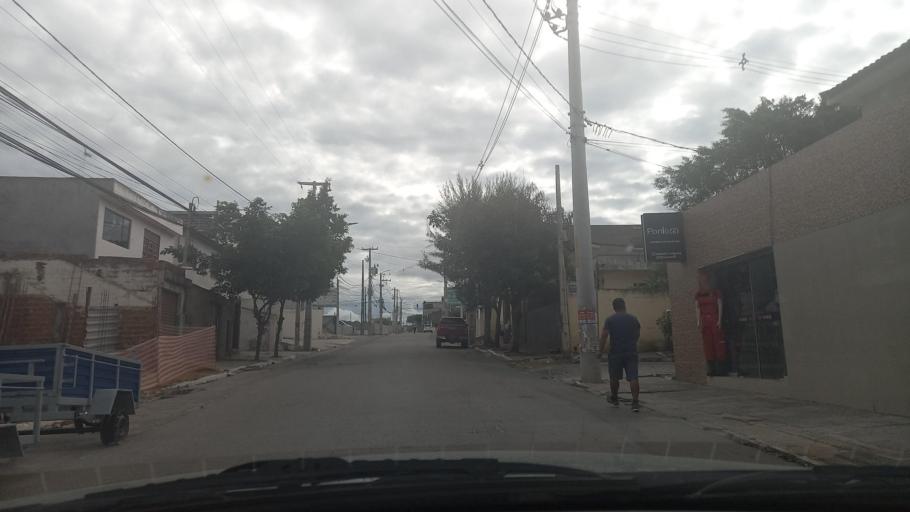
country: BR
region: Pernambuco
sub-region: Caruaru
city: Caruaru
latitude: -8.2864
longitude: -35.9949
